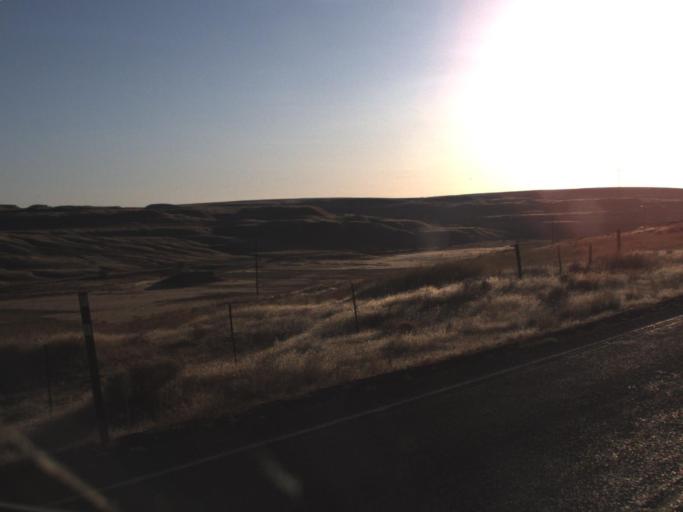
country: US
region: Washington
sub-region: Franklin County
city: Connell
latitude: 46.6509
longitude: -118.5229
